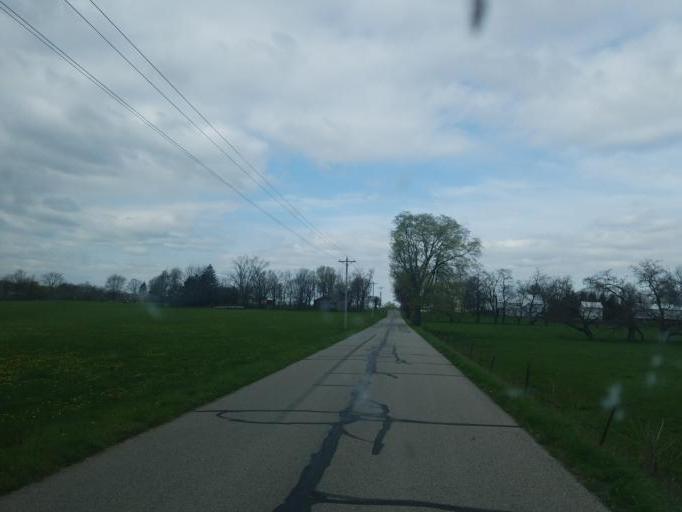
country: US
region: Ohio
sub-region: Morrow County
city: Cardington
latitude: 40.6019
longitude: -82.9742
